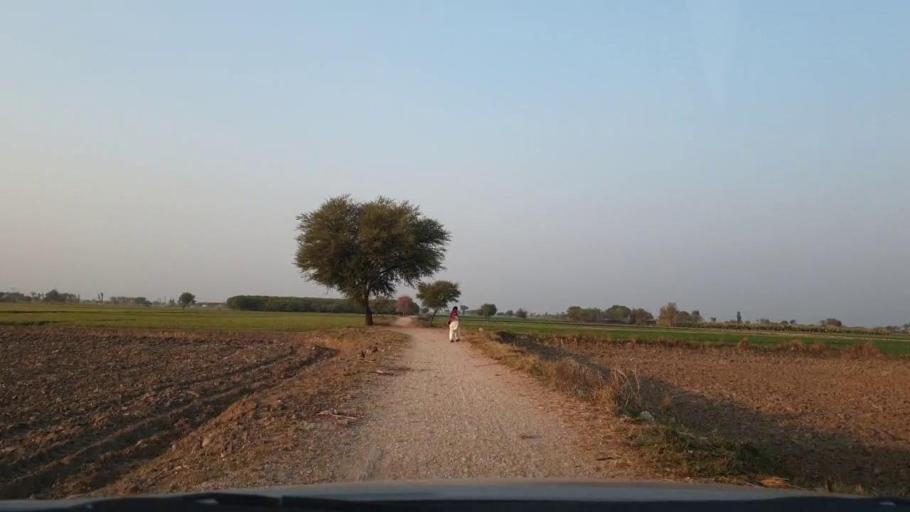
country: PK
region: Sindh
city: Tando Adam
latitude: 25.7153
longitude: 68.5793
